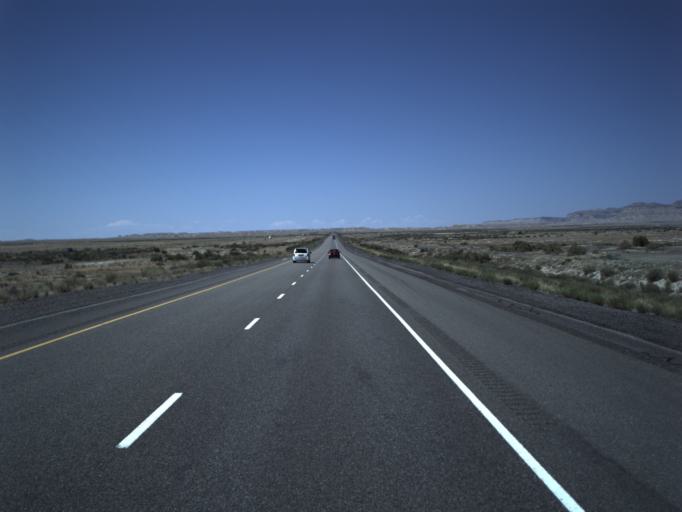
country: US
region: Utah
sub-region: Grand County
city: Moab
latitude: 38.9427
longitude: -109.5546
